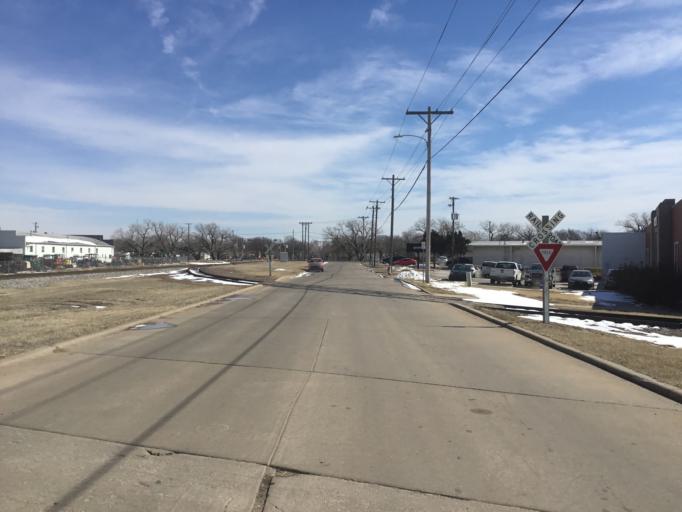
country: US
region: Kansas
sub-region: Sedgwick County
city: Wichita
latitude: 37.6696
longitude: -97.3473
